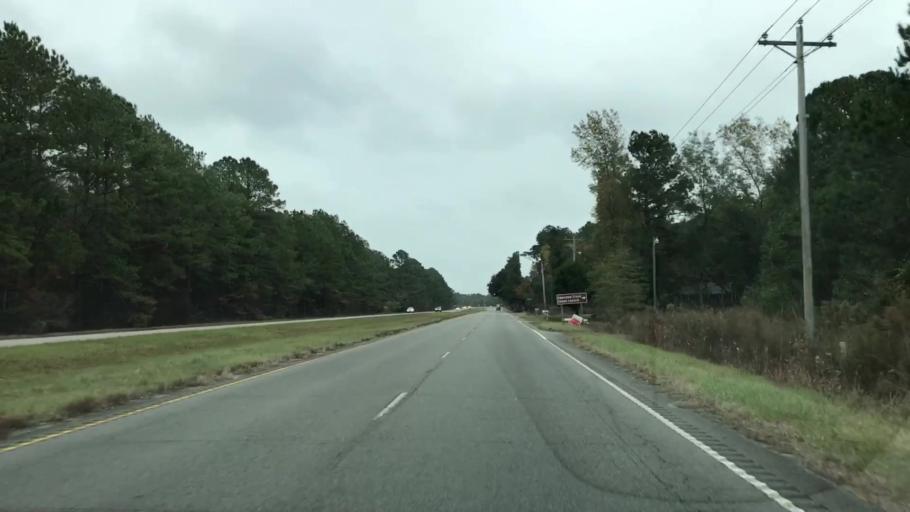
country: US
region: South Carolina
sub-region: Charleston County
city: Awendaw
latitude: 33.0382
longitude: -79.6057
